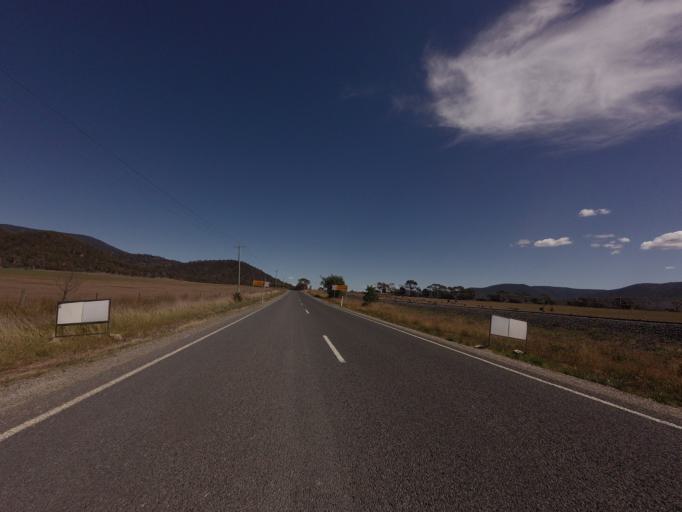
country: AU
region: Tasmania
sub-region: Break O'Day
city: St Helens
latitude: -41.6735
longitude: 147.8982
